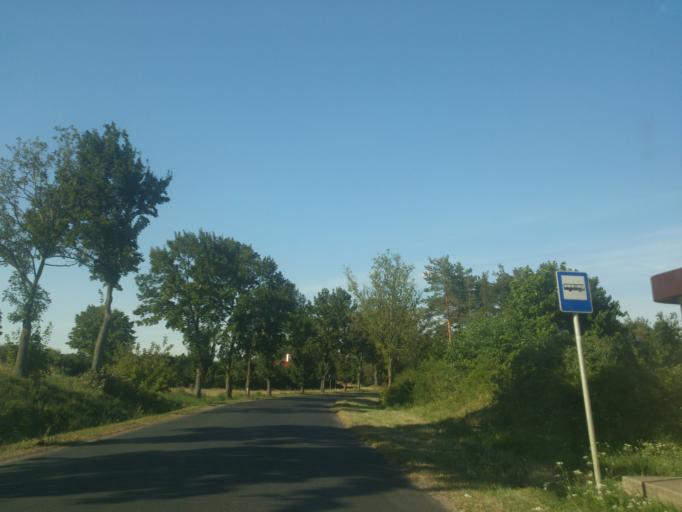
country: PL
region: Kujawsko-Pomorskie
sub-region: Powiat golubsko-dobrzynski
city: Golub-Dobrzyn
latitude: 53.1044
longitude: 19.0237
